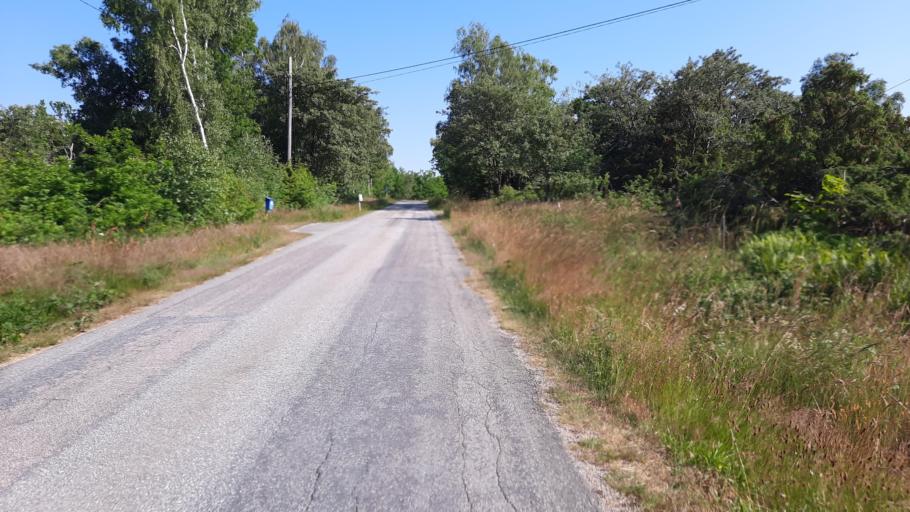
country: SE
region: Blekinge
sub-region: Karlskrona Kommun
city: Sturko
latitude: 56.1236
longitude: 15.6587
